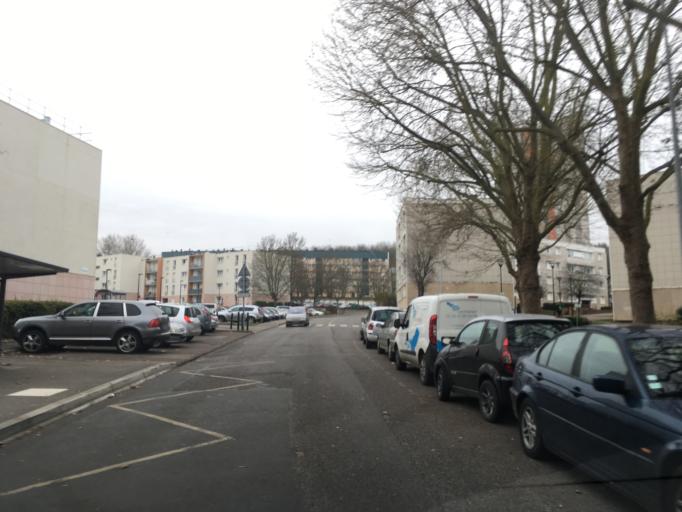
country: FR
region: Haute-Normandie
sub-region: Departement de l'Eure
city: Vernon
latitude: 49.0797
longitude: 1.4837
